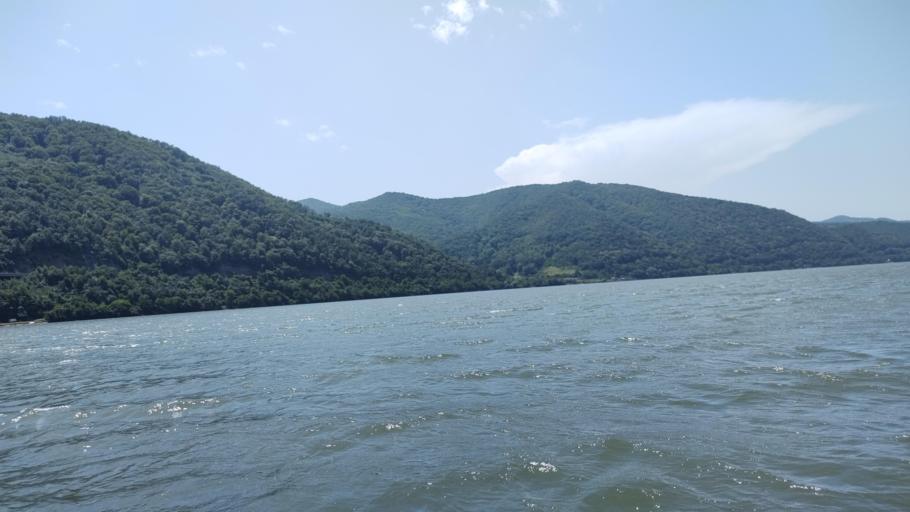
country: RO
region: Caras-Severin
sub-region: Comuna Berzasca
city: Berzasca
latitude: 44.6351
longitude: 21.9727
